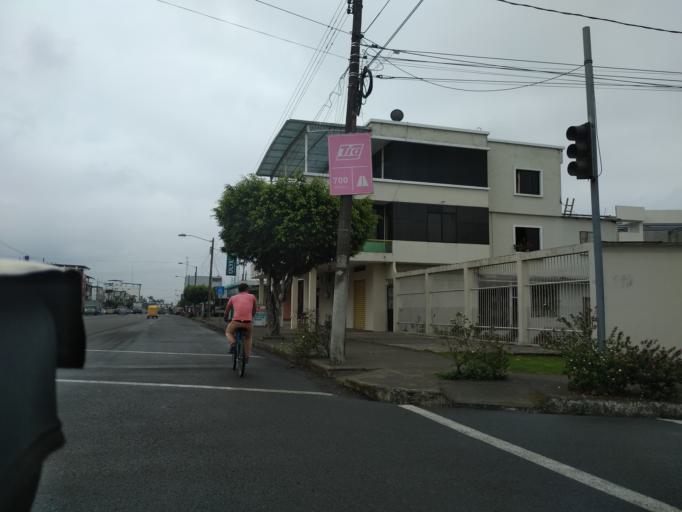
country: EC
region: Cotopaxi
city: La Mana
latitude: -0.9510
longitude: -79.3478
